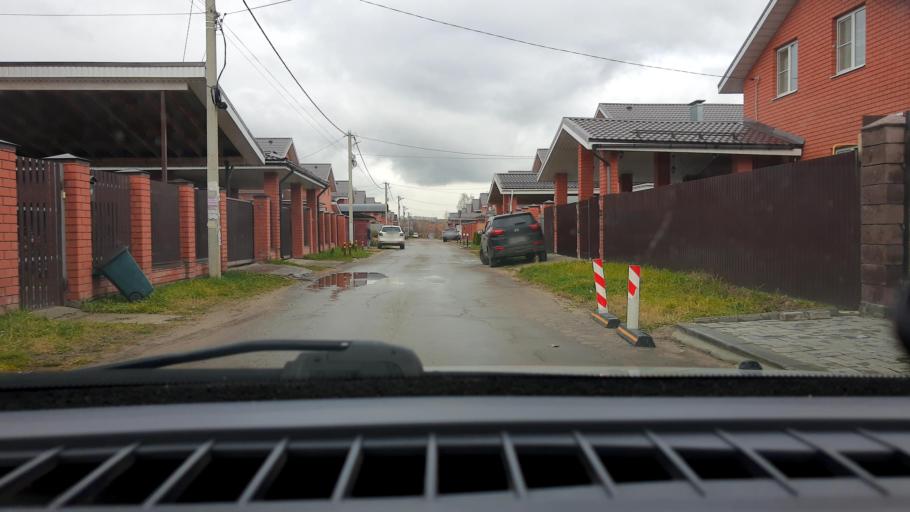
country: RU
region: Nizjnij Novgorod
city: Afonino
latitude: 56.2028
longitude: 44.1266
